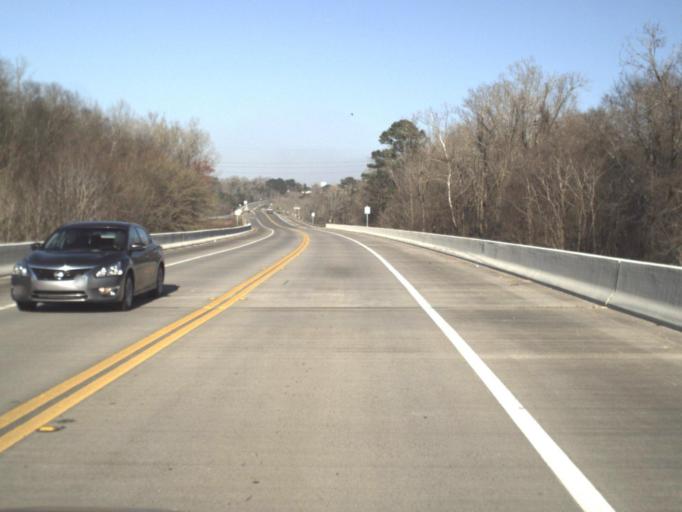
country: US
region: Florida
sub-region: Gadsden County
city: Chattahoochee
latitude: 30.6989
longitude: -84.8640
